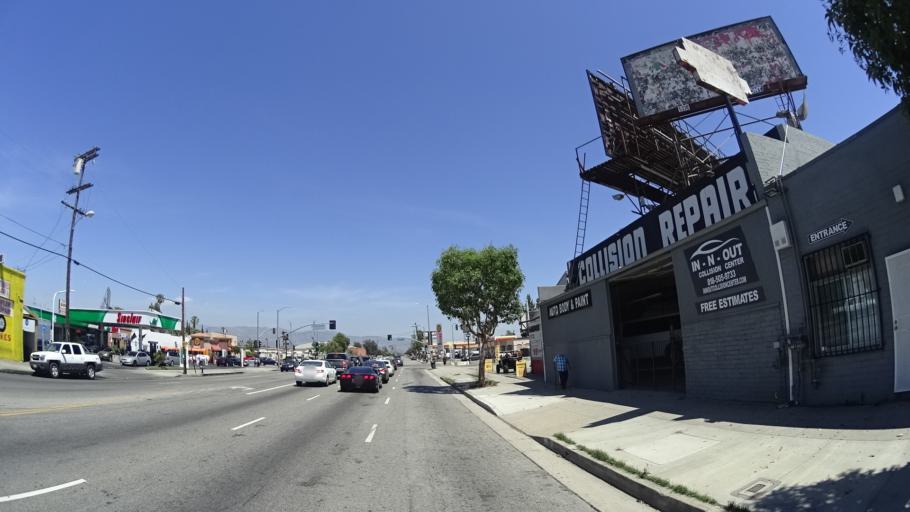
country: US
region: California
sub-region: Los Angeles County
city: North Hollywood
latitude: 34.1867
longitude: -118.3888
